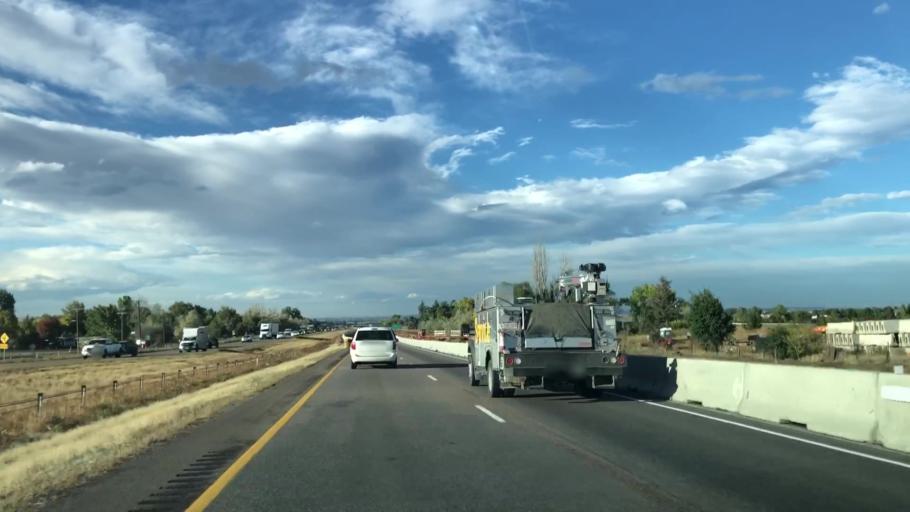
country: US
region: Colorado
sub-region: Weld County
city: Windsor
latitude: 40.4631
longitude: -104.9916
